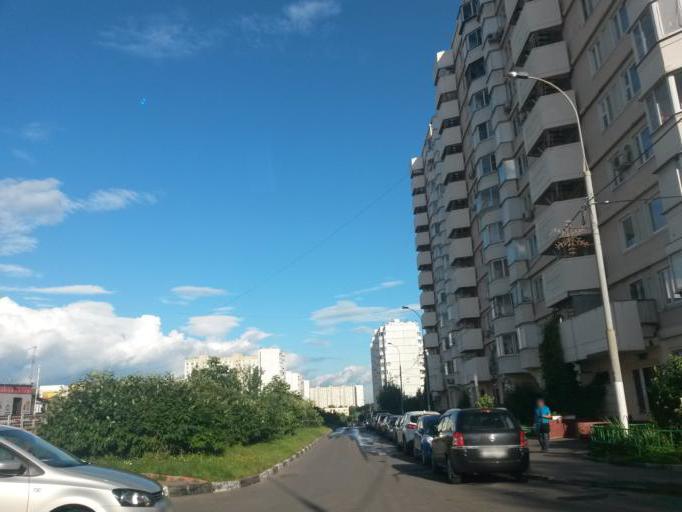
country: RU
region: Moscow
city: Chertanovo Yuzhnoye
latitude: 55.5696
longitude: 37.5681
